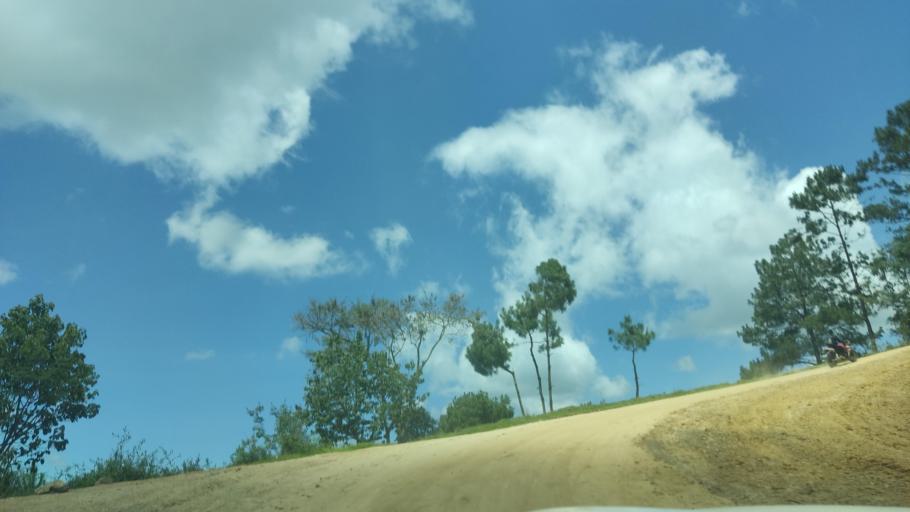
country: GT
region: Chimaltenango
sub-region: Municipio de San Juan Comalapa
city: Comalapa
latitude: 14.7786
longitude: -90.8759
